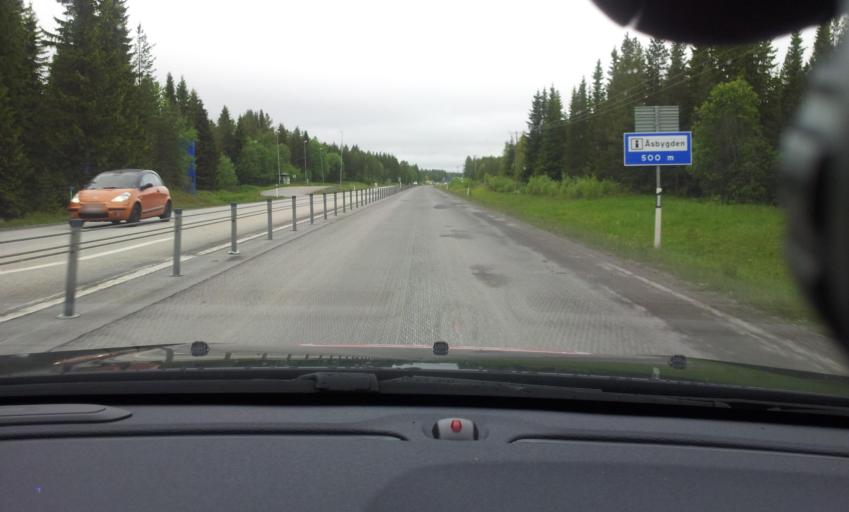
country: SE
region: Jaemtland
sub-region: OEstersunds Kommun
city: Ostersund
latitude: 63.2276
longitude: 14.6183
